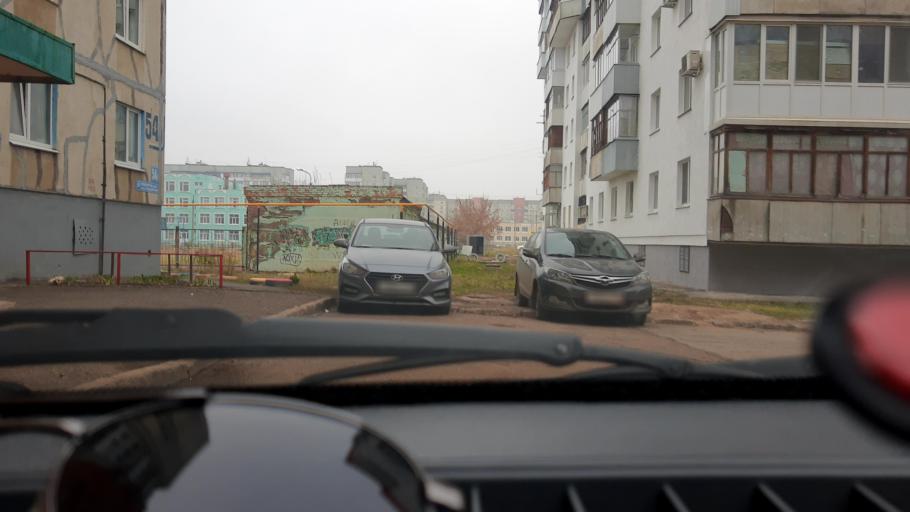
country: RU
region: Bashkortostan
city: Iglino
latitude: 54.7684
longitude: 56.2304
